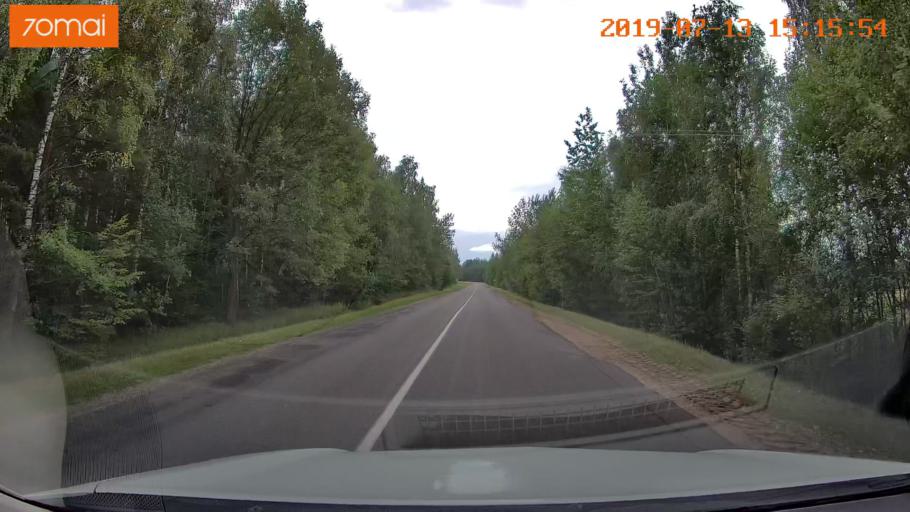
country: BY
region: Mogilev
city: Hlusha
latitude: 53.1135
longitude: 28.8290
